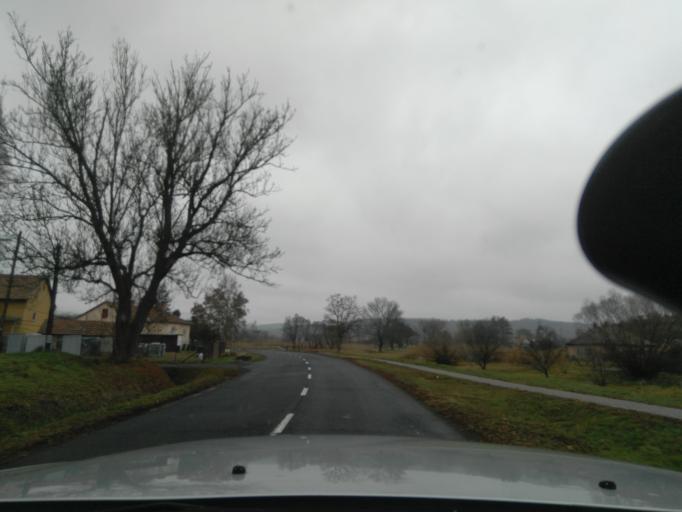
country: HU
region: Nograd
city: Kazar
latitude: 48.0314
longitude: 19.8726
